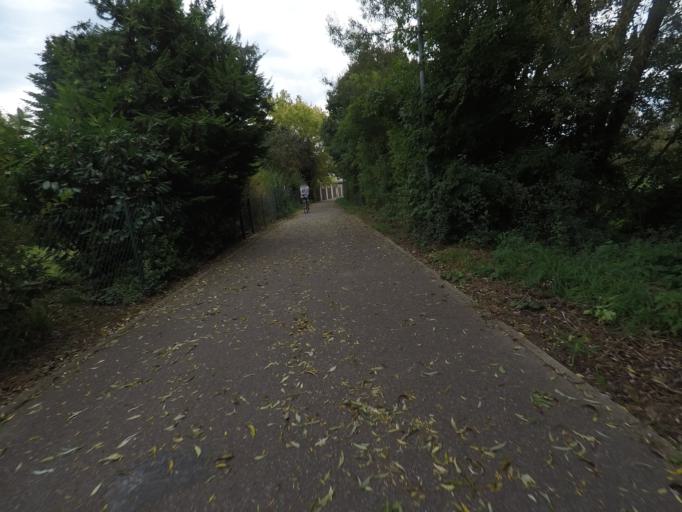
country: DE
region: Baden-Wuerttemberg
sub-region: Regierungsbezirk Stuttgart
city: Herrenberg
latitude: 48.5722
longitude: 8.8796
